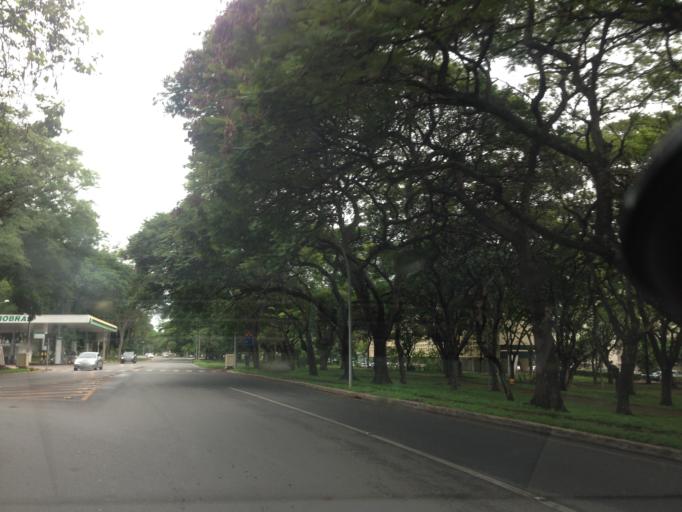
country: BR
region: Federal District
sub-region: Brasilia
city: Brasilia
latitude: -15.8128
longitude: -47.9008
